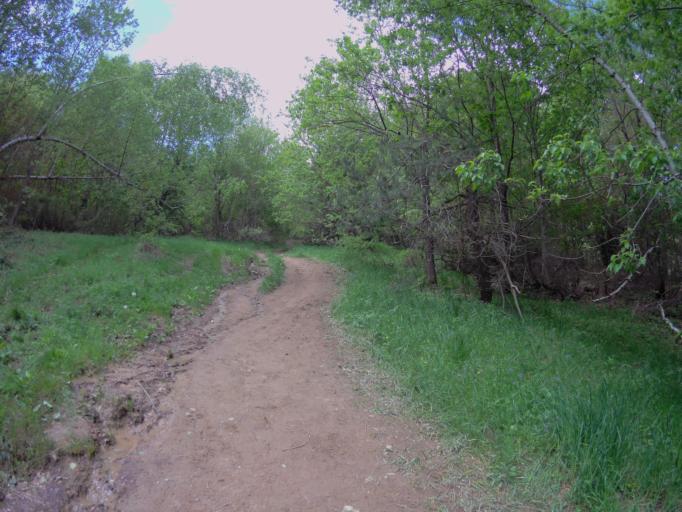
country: PL
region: Subcarpathian Voivodeship
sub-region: Powiat bieszczadzki
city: Lutowiska
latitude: 49.1448
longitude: 22.5633
